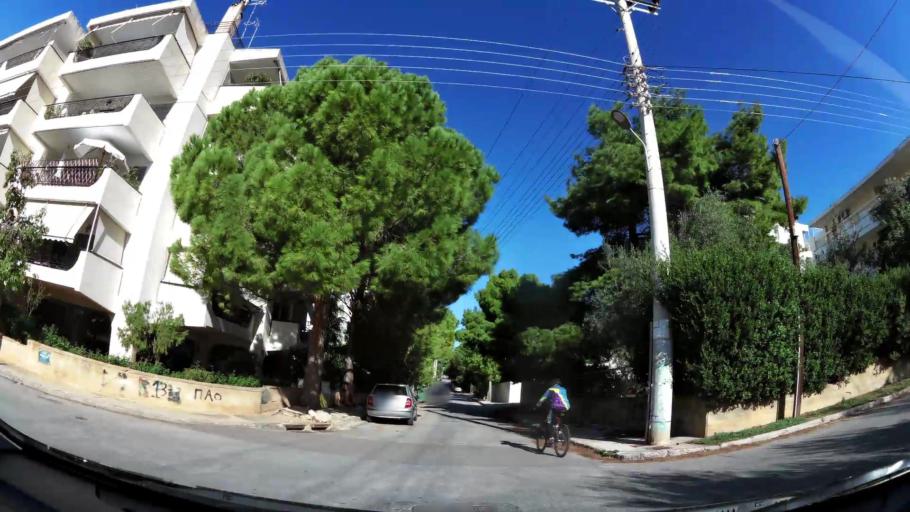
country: GR
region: Attica
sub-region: Nomarchia Athinas
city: Glyfada
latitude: 37.8674
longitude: 23.7694
